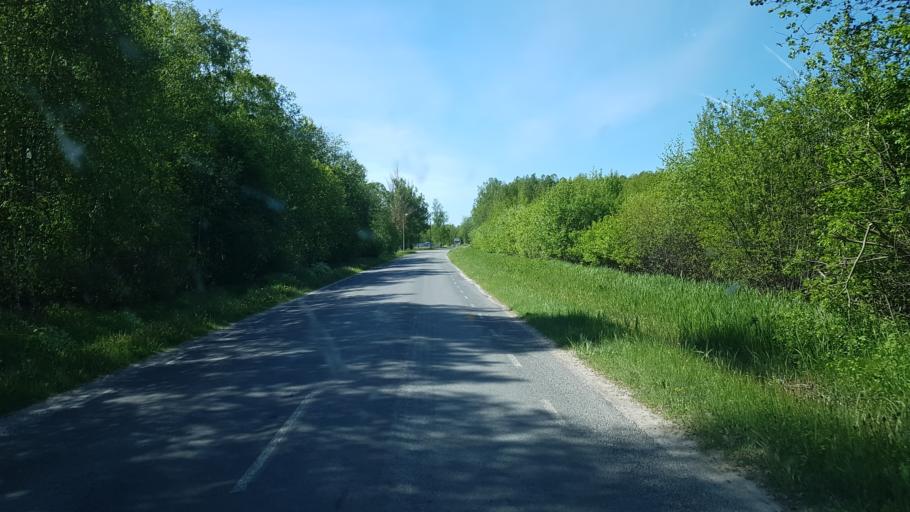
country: EE
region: Saare
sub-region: Kuressaare linn
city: Kuressaare
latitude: 58.2745
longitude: 22.4984
